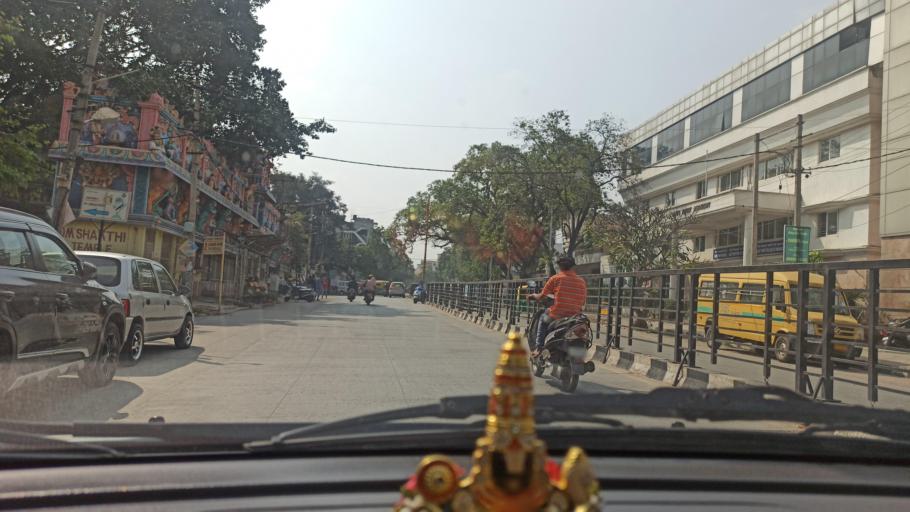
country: IN
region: Karnataka
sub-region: Bangalore Urban
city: Bangalore
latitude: 13.0167
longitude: 77.6436
